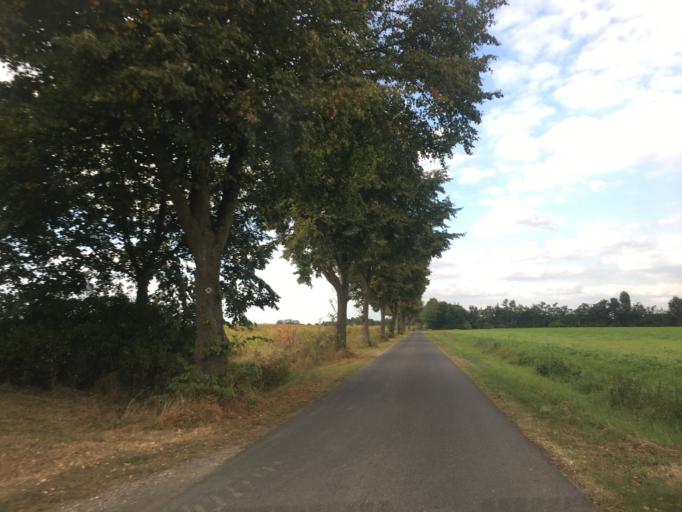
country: DE
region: North Rhine-Westphalia
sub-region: Regierungsbezirk Munster
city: Muenster
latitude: 51.9755
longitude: 7.5339
